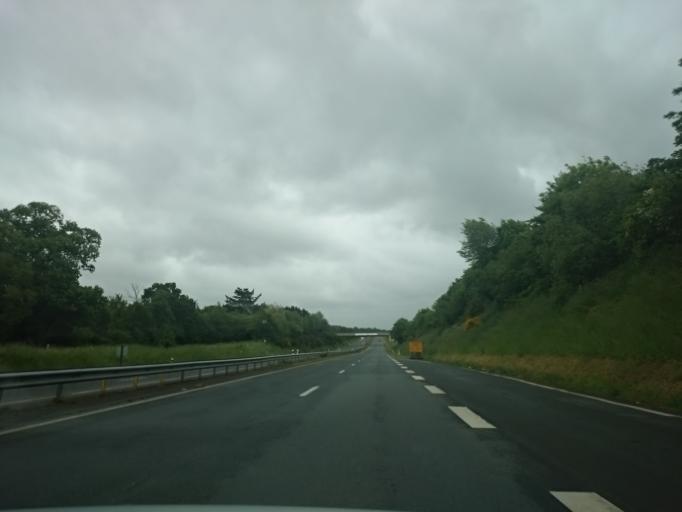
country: FR
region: Brittany
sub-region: Departement des Cotes-d'Armor
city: Begard
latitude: 48.6350
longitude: -3.3234
